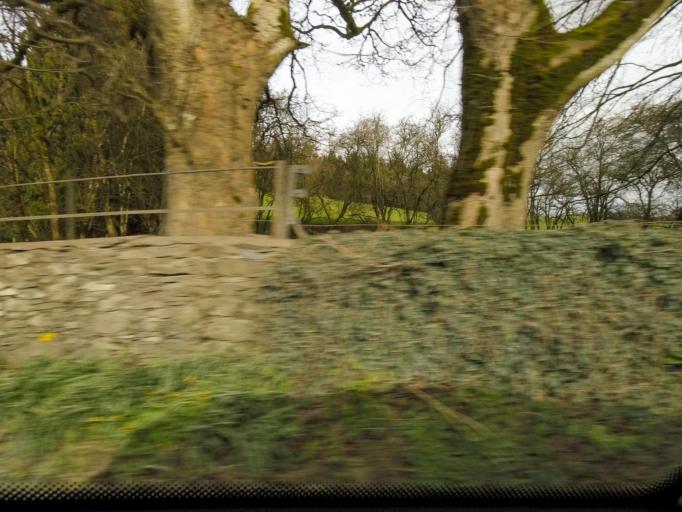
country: IE
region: Leinster
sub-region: Wicklow
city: Blessington
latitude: 53.1767
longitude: -6.5594
